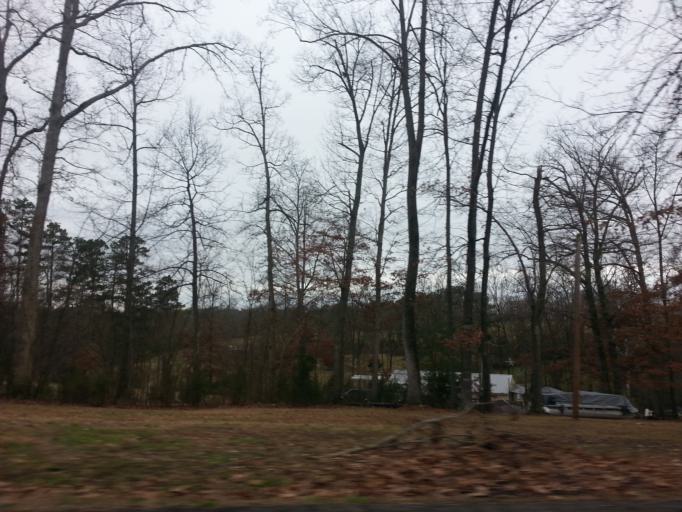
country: US
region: Tennessee
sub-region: Jefferson County
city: Jefferson City
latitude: 36.1474
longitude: -83.4851
